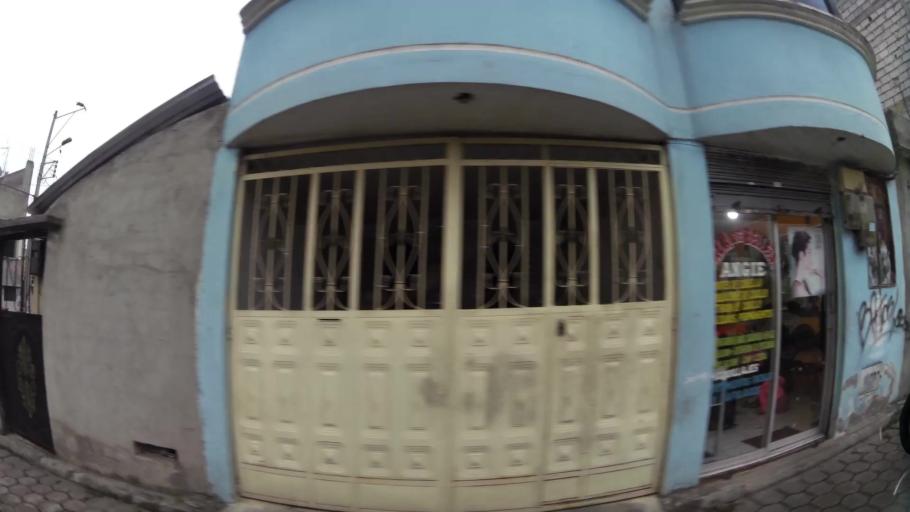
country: EC
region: Pichincha
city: Quito
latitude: -0.3135
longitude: -78.5466
